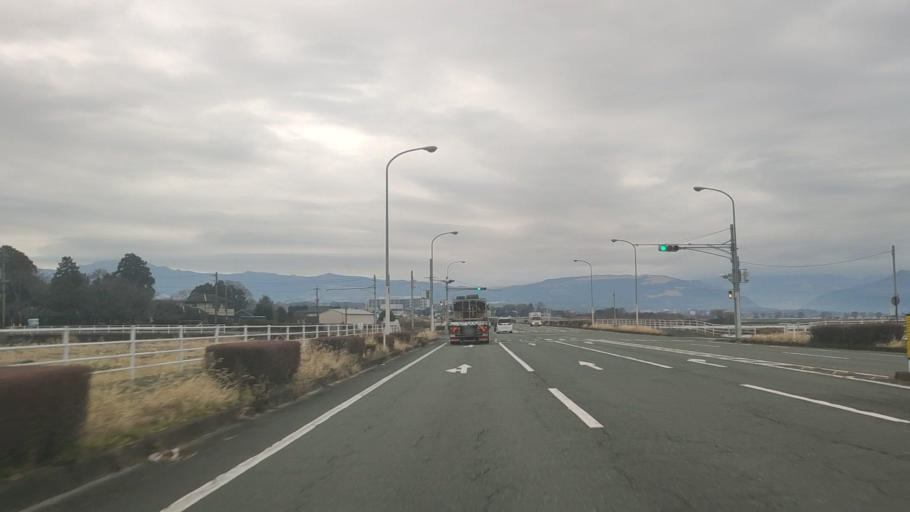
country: JP
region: Kumamoto
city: Ozu
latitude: 32.8684
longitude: 130.8383
